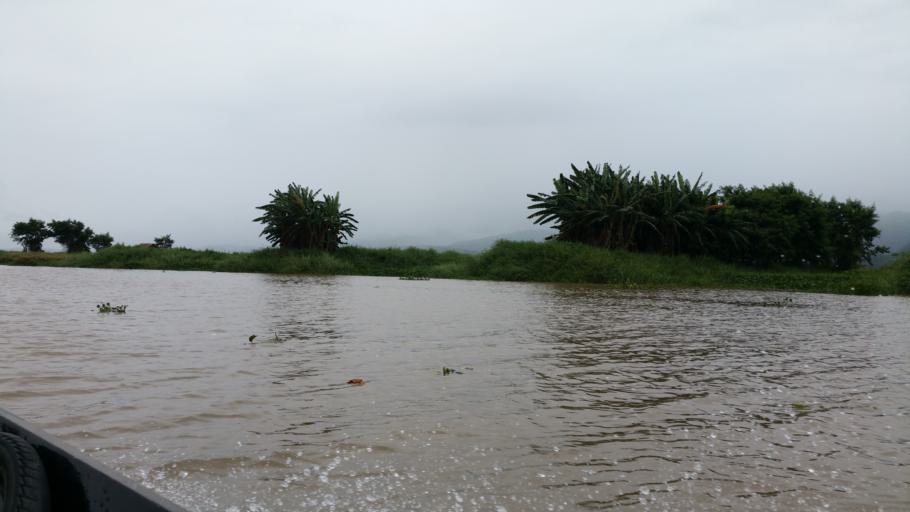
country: MM
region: Shan
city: Taunggyi
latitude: 20.6212
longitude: 96.9203
